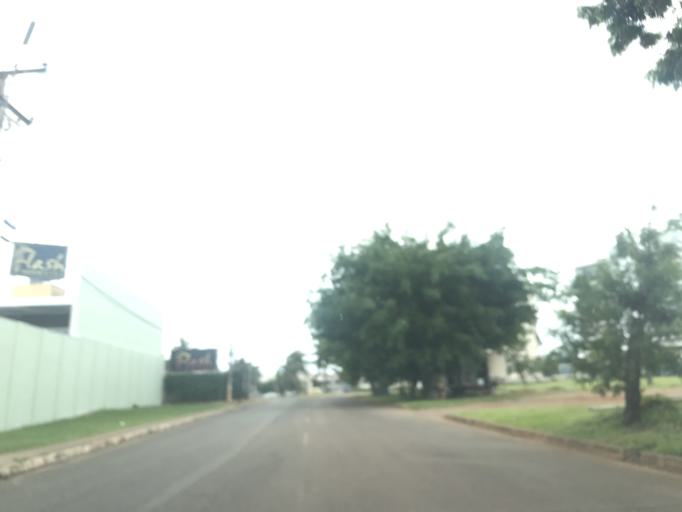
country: BR
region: Federal District
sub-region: Brasilia
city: Brasilia
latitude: -15.8732
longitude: -48.0339
